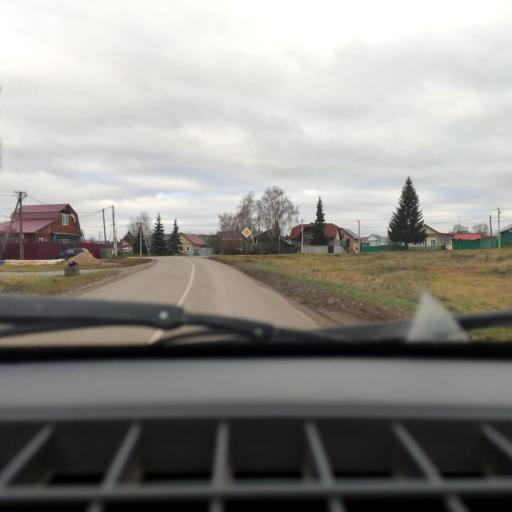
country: RU
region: Bashkortostan
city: Avdon
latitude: 54.6536
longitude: 55.7773
